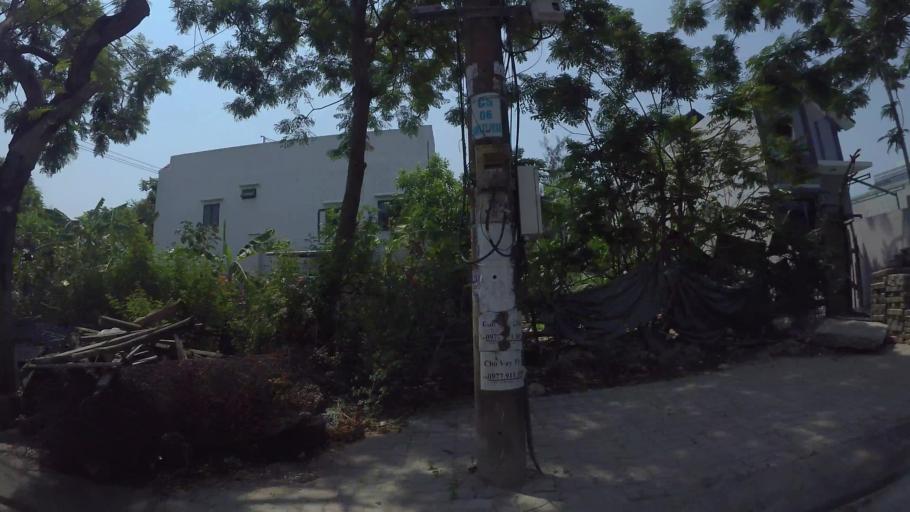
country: VN
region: Da Nang
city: Ngu Hanh Son
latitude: 15.9934
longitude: 108.2564
